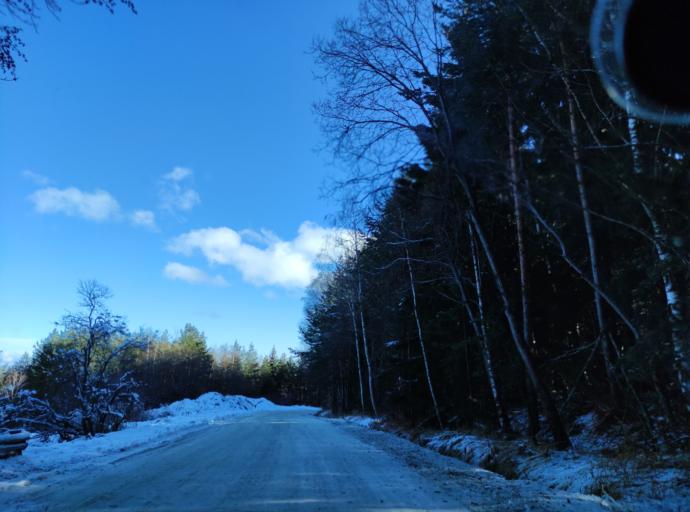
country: BG
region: Sofia-Capital
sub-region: Stolichna Obshtina
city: Sofia
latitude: 42.6040
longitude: 23.3057
